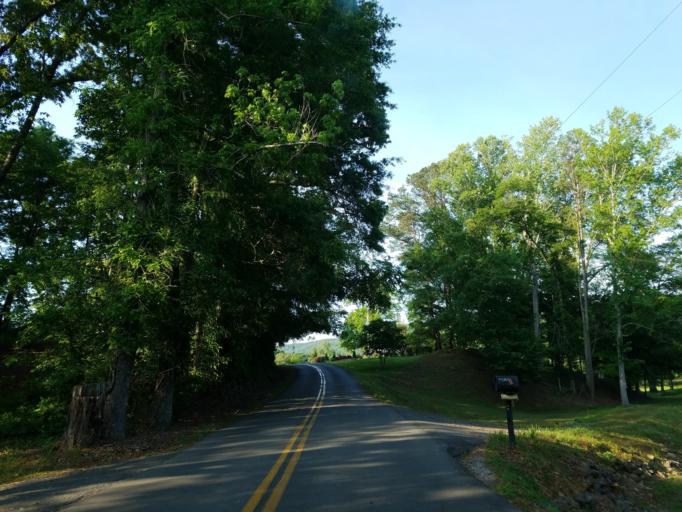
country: US
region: Georgia
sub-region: Gordon County
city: Calhoun
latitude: 34.5356
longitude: -85.1081
